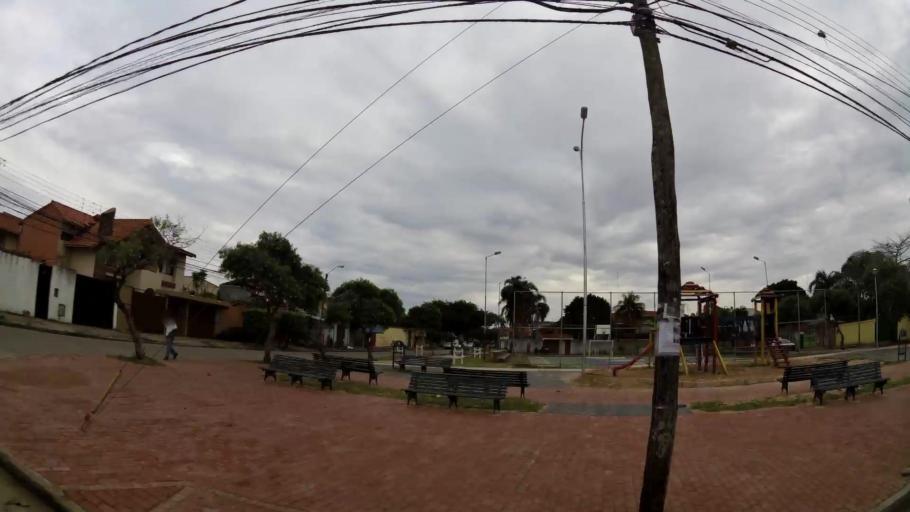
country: BO
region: Santa Cruz
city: Santa Cruz de la Sierra
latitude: -17.7677
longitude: -63.1611
